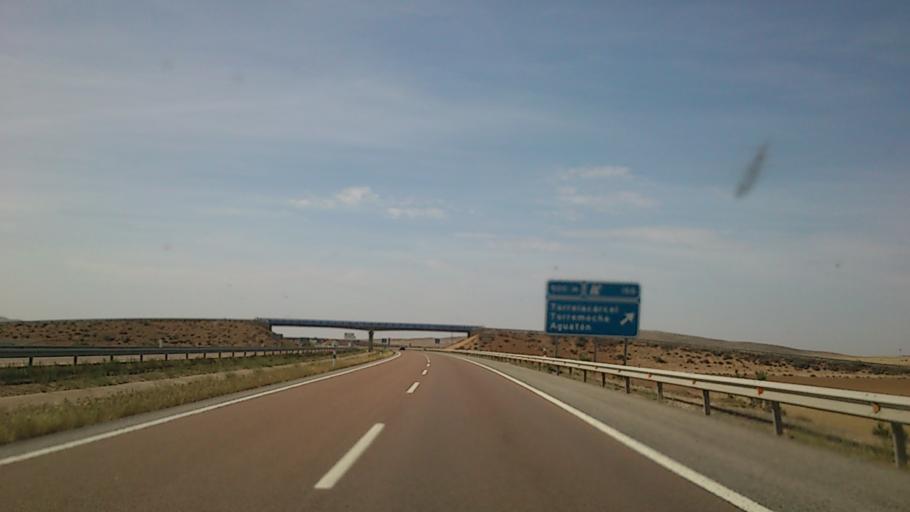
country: ES
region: Aragon
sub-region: Provincia de Teruel
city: Singra
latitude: 40.6132
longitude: -1.2888
